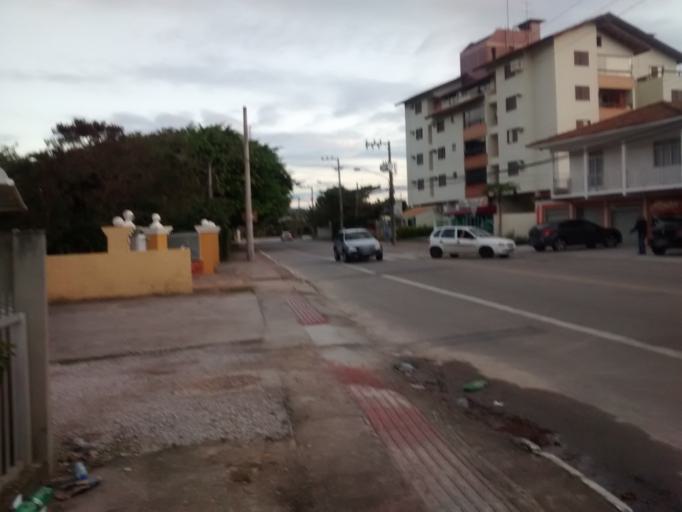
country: BR
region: Santa Catarina
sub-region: Florianopolis
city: Itacorubi
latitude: -27.4156
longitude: -48.4256
